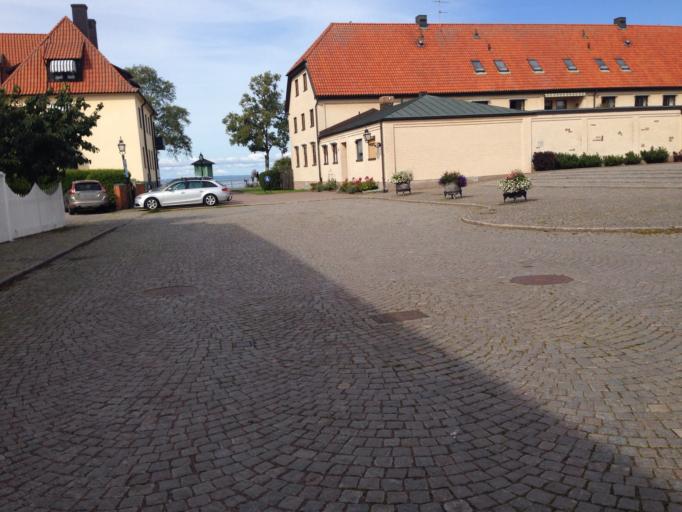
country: SE
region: OEstergoetland
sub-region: Vadstena Kommun
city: Vadstena
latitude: 58.4490
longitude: 14.8882
